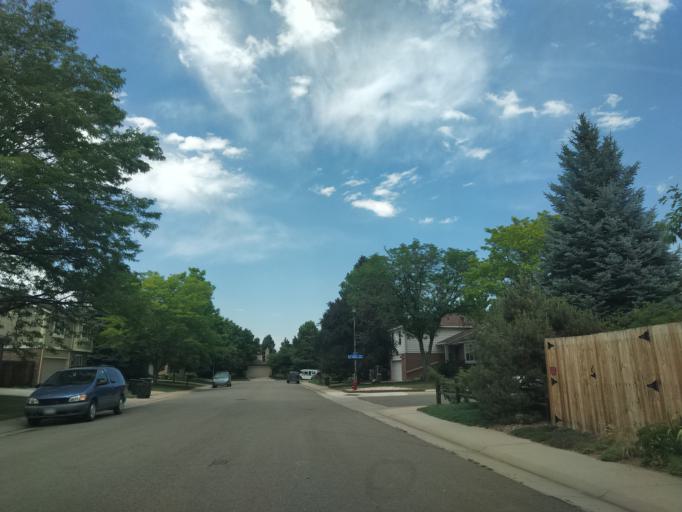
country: US
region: Colorado
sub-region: Jefferson County
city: Lakewood
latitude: 39.6765
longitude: -105.1045
